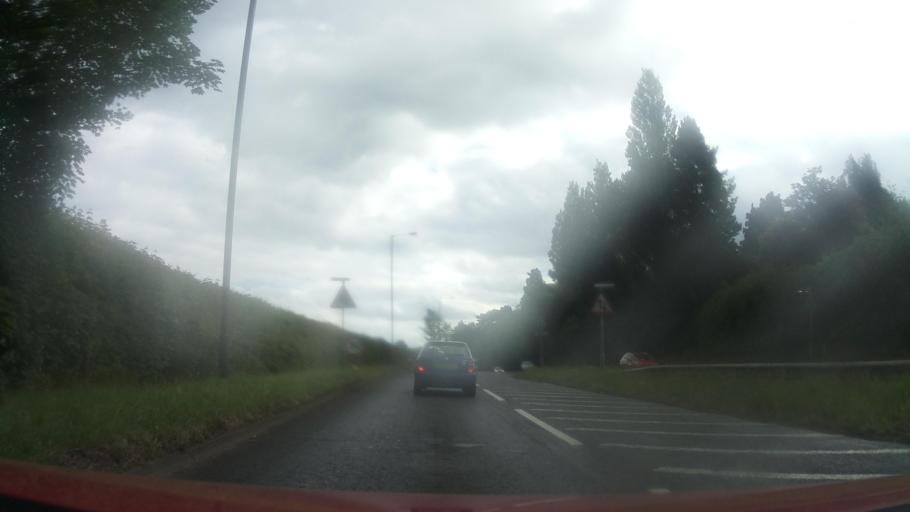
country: GB
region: England
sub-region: Dudley
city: Kingswinford
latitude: 52.5332
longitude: -2.1777
